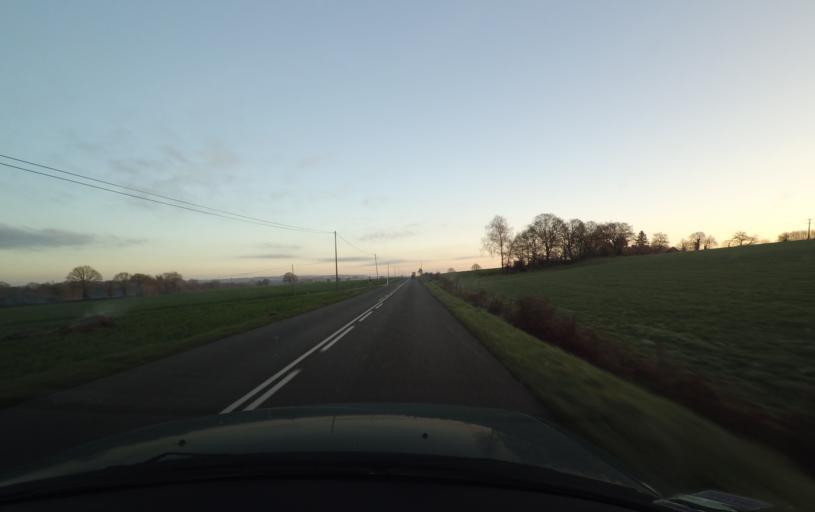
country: FR
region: Pays de la Loire
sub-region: Departement de la Mayenne
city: Villaines-la-Juhel
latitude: 48.3201
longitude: -0.3168
